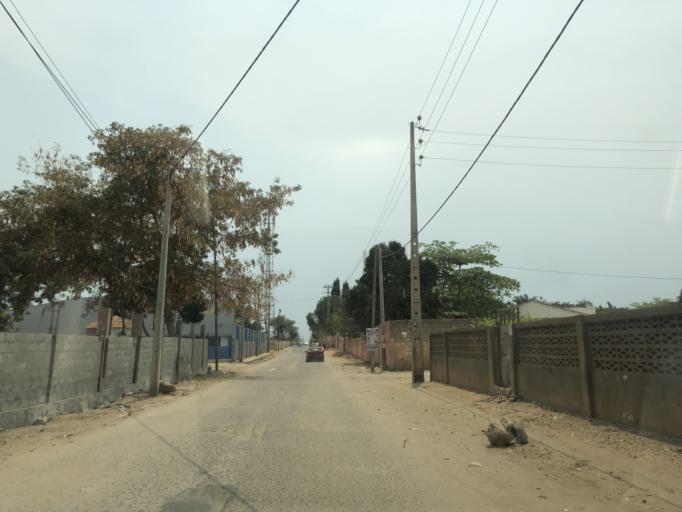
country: AO
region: Luanda
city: Luanda
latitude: -8.8894
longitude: 13.1972
